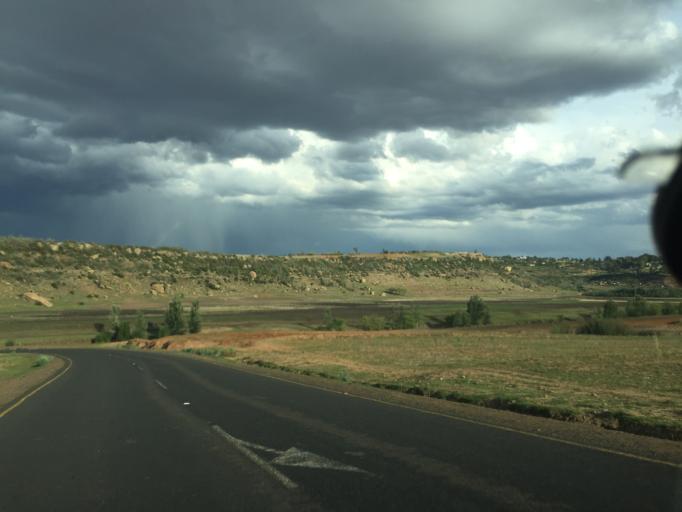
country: LS
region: Berea
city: Teyateyaneng
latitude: -29.0916
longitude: 27.9414
